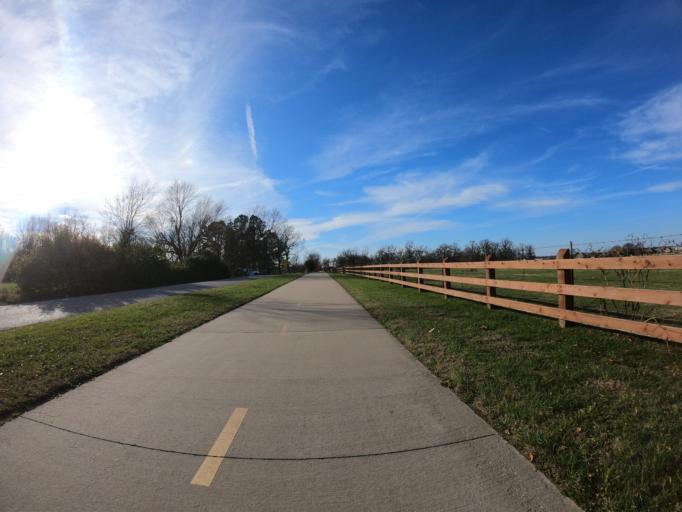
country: US
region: Arkansas
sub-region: Benton County
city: Lowell
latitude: 36.2657
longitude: -94.1584
